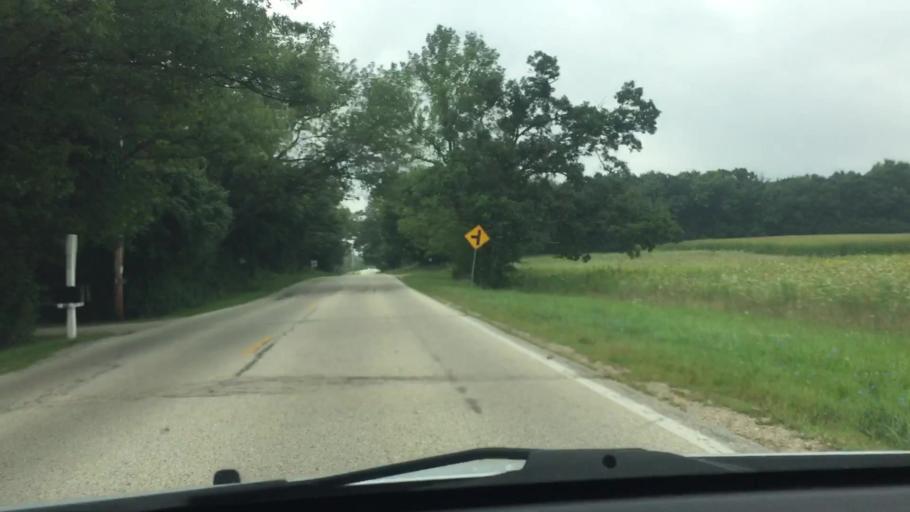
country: US
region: Wisconsin
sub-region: Waukesha County
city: Dousman
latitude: 43.0422
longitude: -88.4425
